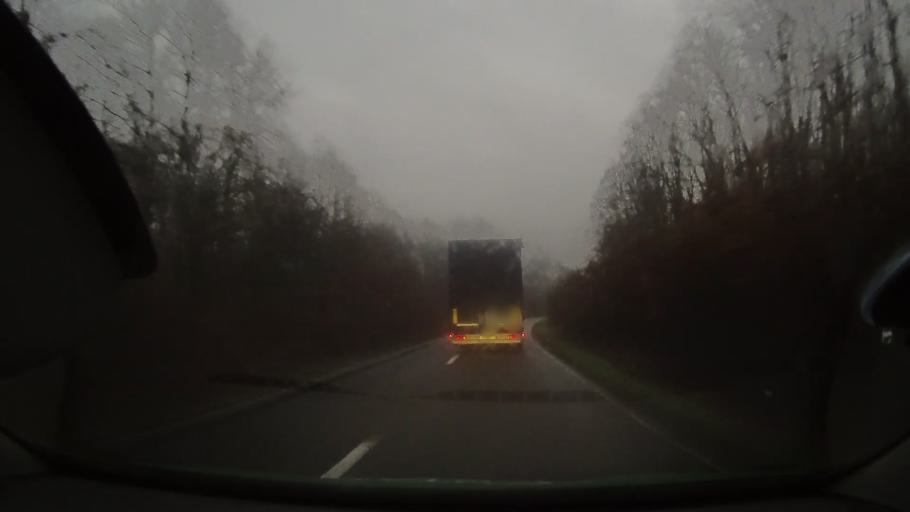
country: RO
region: Arad
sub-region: Comuna Beliu
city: Beliu
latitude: 46.5048
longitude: 21.9719
